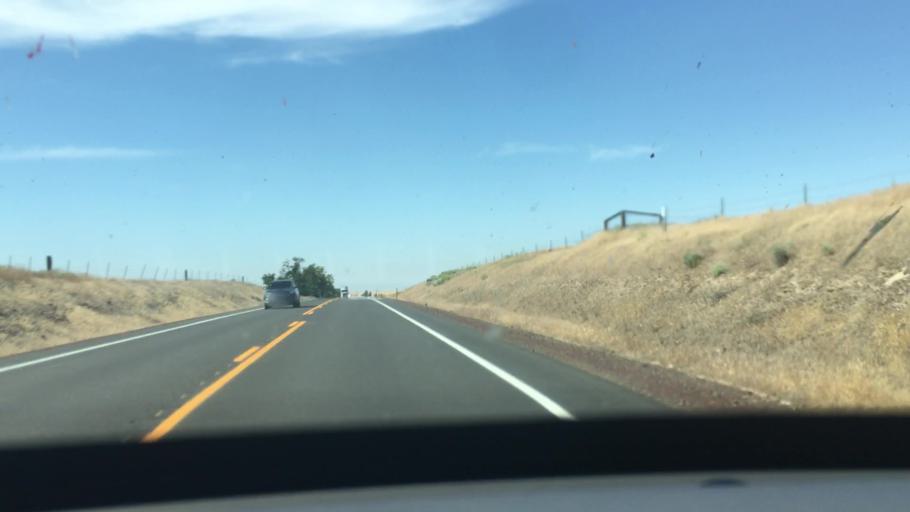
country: US
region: Oregon
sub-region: Sherman County
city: Moro
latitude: 45.3156
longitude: -120.7686
